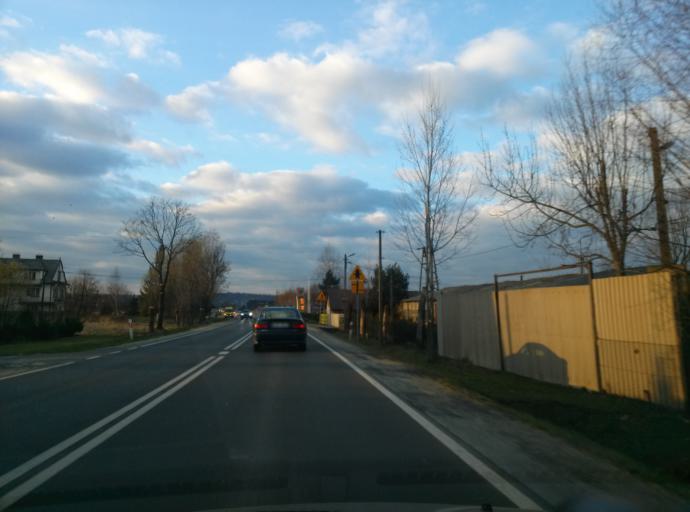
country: PL
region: Lesser Poland Voivodeship
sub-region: Powiat brzeski
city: Gnojnik
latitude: 49.9041
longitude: 20.6058
